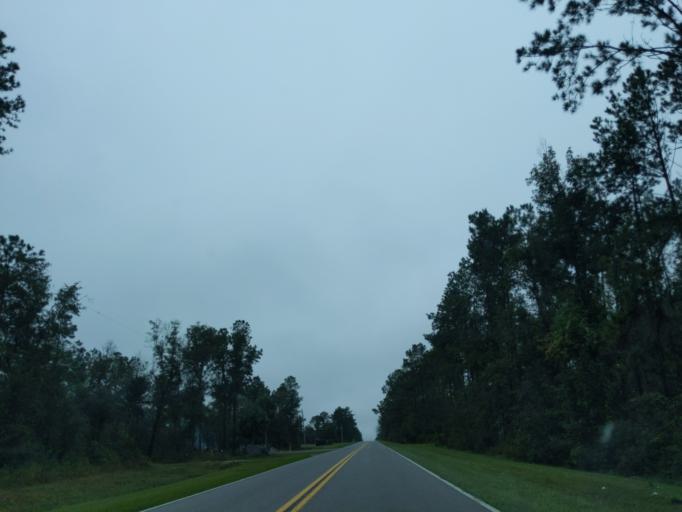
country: US
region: Florida
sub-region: Jackson County
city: Sneads
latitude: 30.6493
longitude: -84.9389
